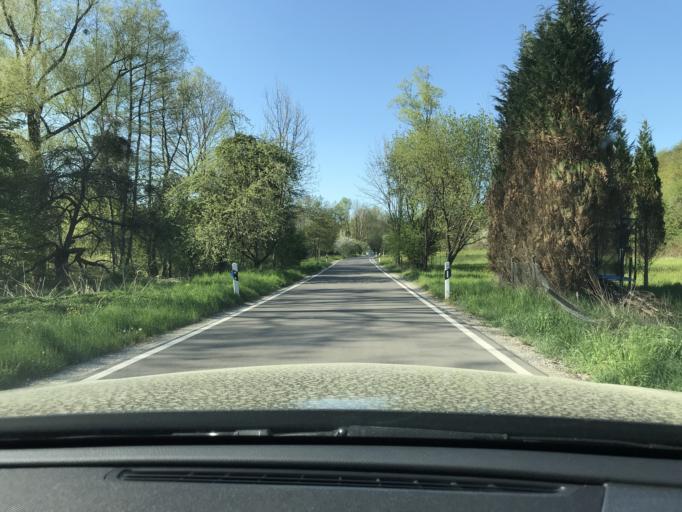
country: DE
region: Baden-Wuerttemberg
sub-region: Regierungsbezirk Stuttgart
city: Baltmannsweiler
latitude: 48.7739
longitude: 9.4139
